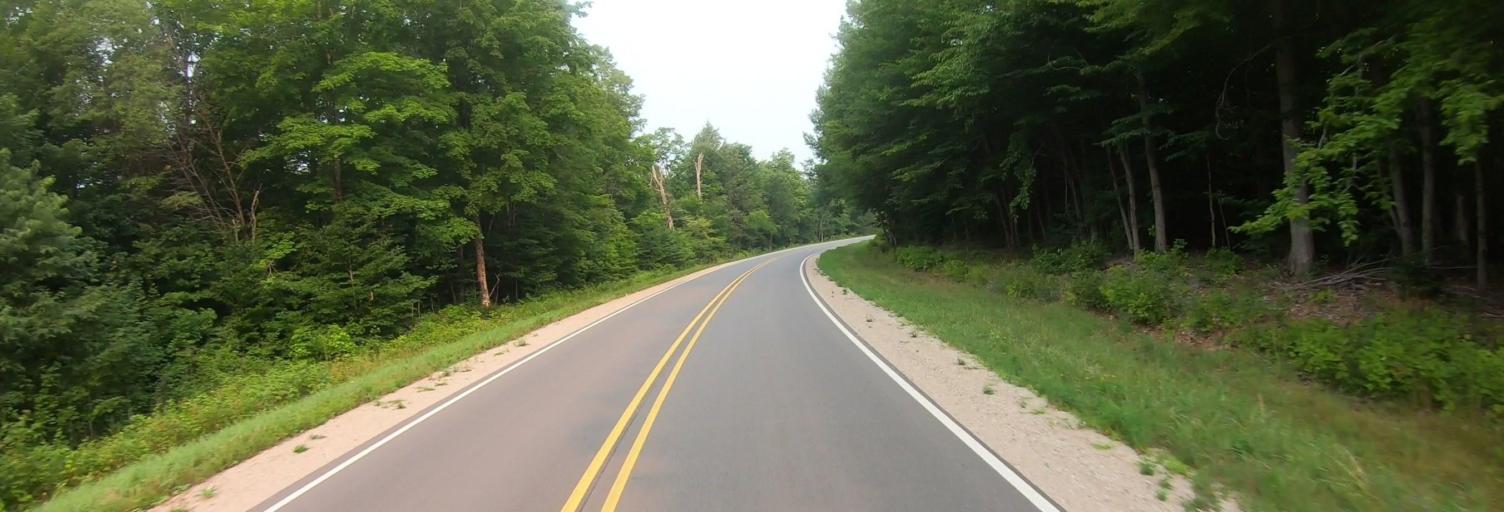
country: US
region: Michigan
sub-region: Luce County
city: Newberry
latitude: 46.4807
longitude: -85.0773
